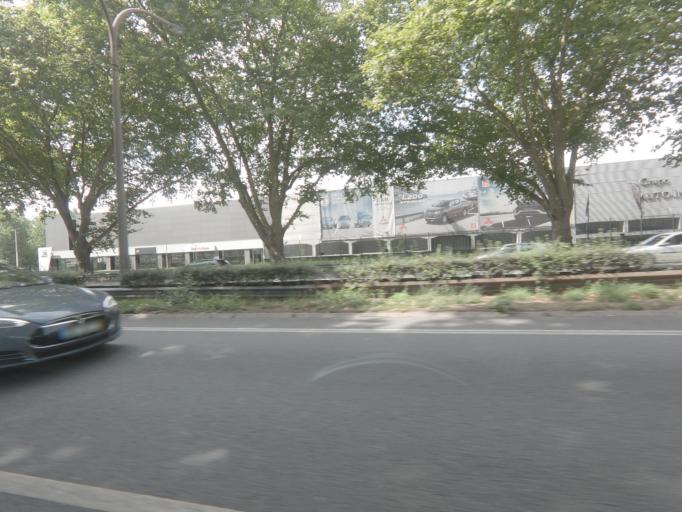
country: PT
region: Porto
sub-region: Matosinhos
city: Senhora da Hora
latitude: 41.1703
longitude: -8.6460
